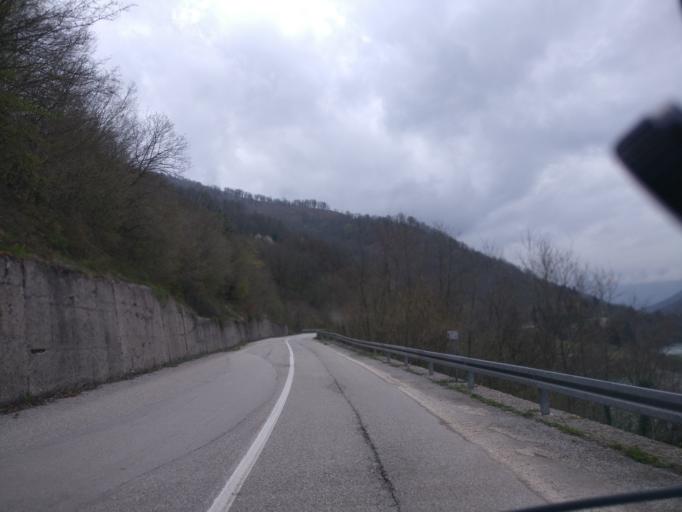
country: BA
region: Republika Srpska
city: Foca
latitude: 43.4542
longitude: 18.7524
